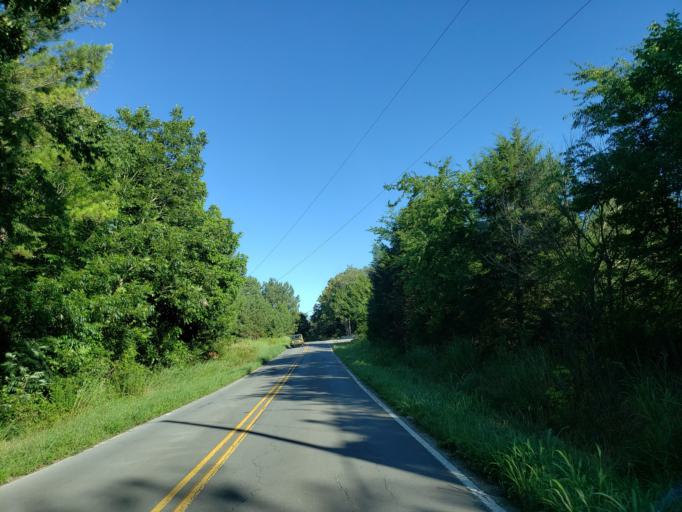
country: US
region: Georgia
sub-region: Polk County
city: Aragon
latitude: 34.1117
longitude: -85.0326
